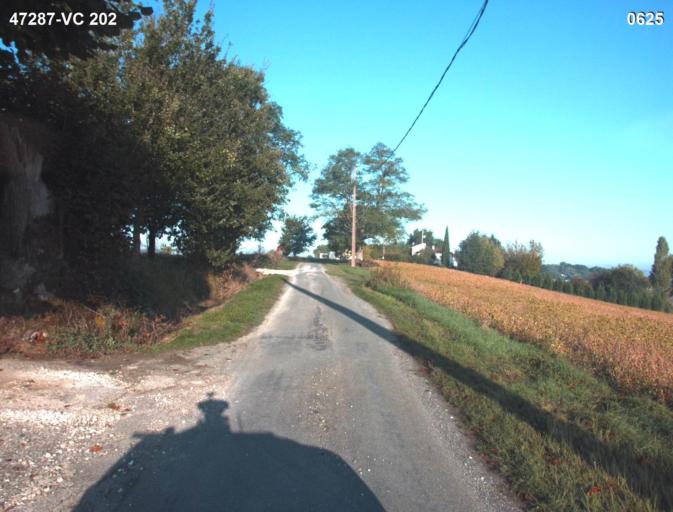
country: FR
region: Aquitaine
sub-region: Departement du Lot-et-Garonne
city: Laplume
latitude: 44.1154
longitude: 0.4639
